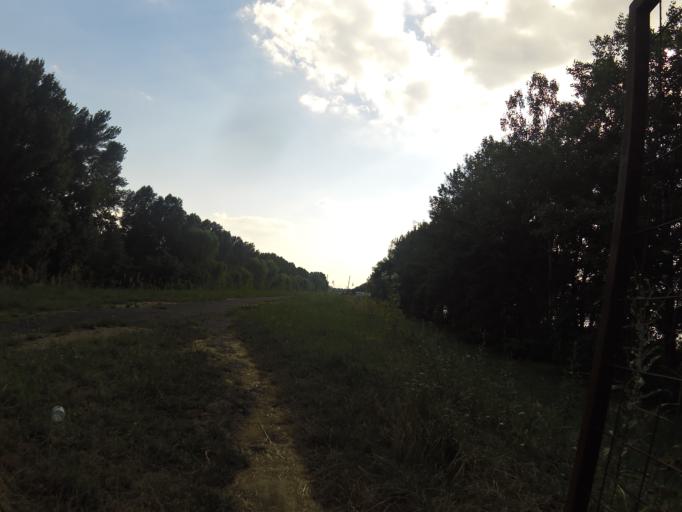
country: HU
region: Jasz-Nagykun-Szolnok
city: Abadszalok
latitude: 47.4851
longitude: 20.5920
